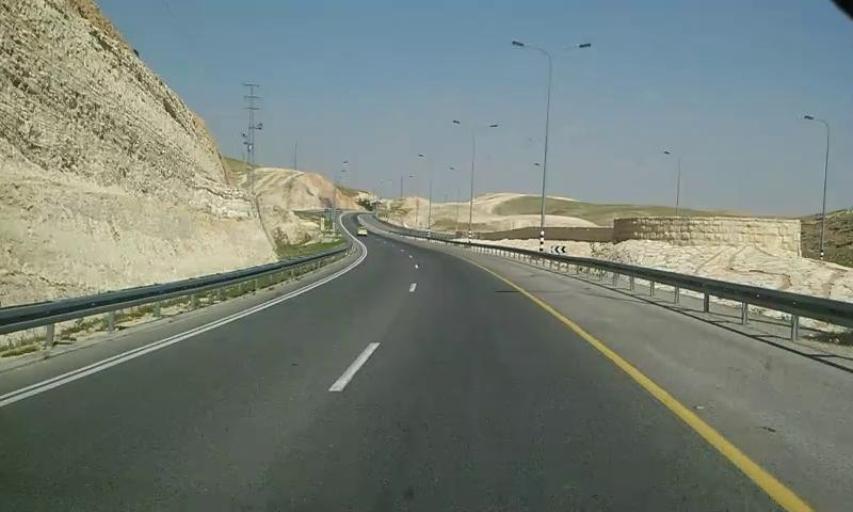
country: PS
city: Az Za`ayyim
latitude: 31.8099
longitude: 35.3395
